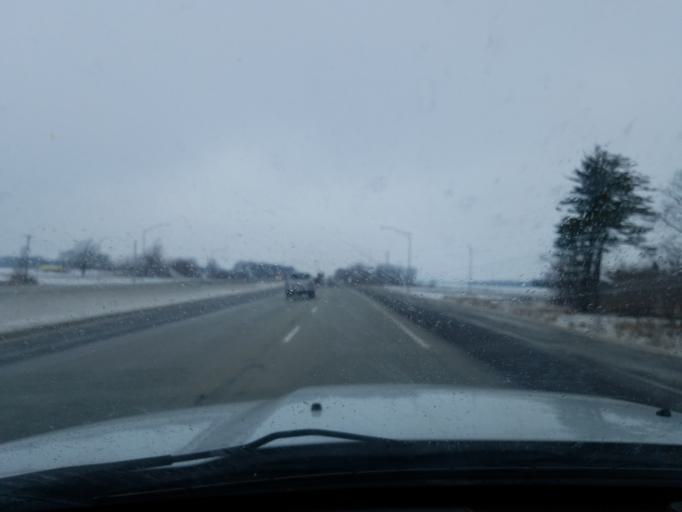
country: US
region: Indiana
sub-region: Marshall County
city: Argos
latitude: 41.1712
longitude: -86.2411
